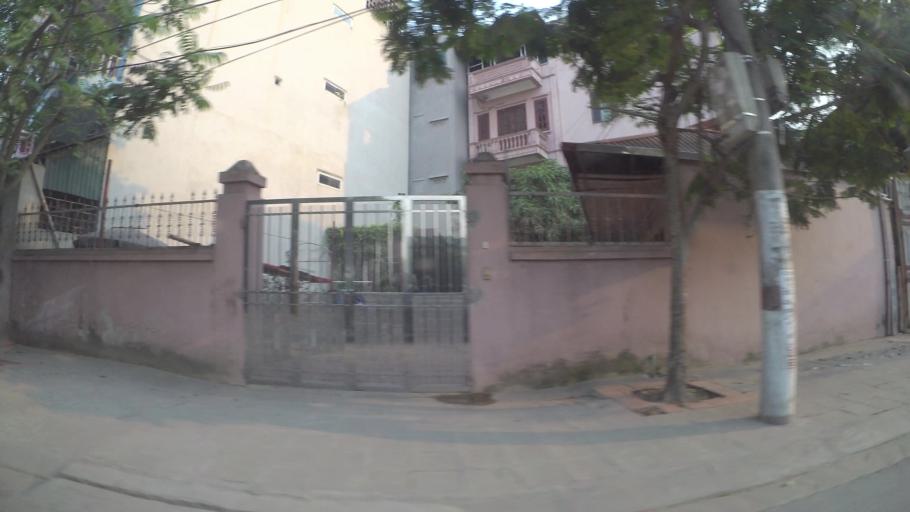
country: VN
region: Ha Noi
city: Van Dien
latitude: 20.9230
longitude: 105.8443
